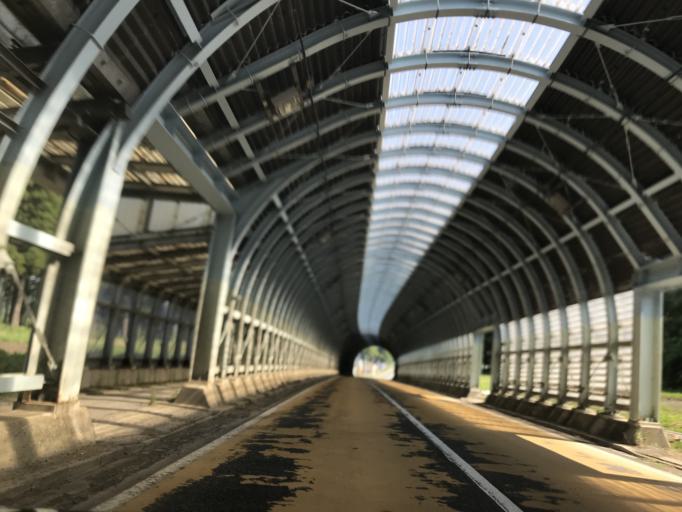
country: JP
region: Akita
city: Yokotemachi
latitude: 39.4174
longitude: 140.7472
